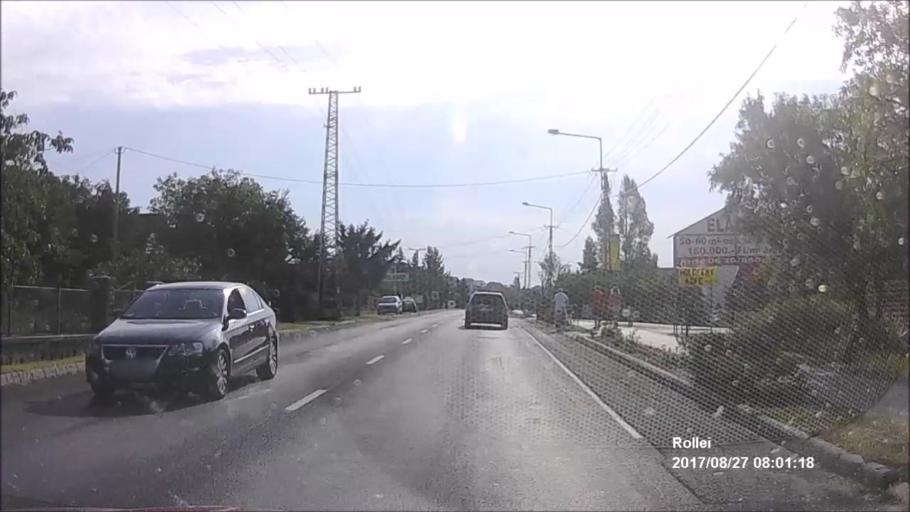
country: HU
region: Zala
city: Vonyarcvashegy
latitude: 46.7629
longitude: 17.3104
